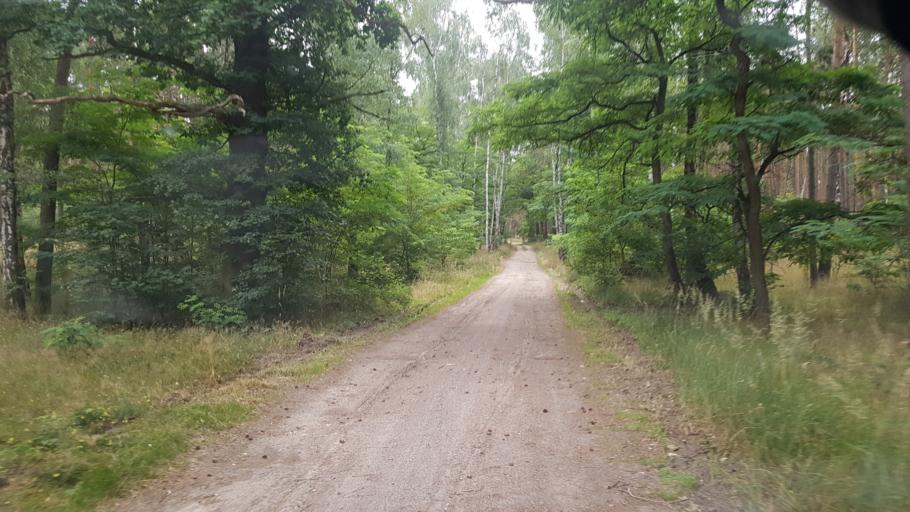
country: DE
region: Brandenburg
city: Lebusa
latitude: 51.7783
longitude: 13.3860
